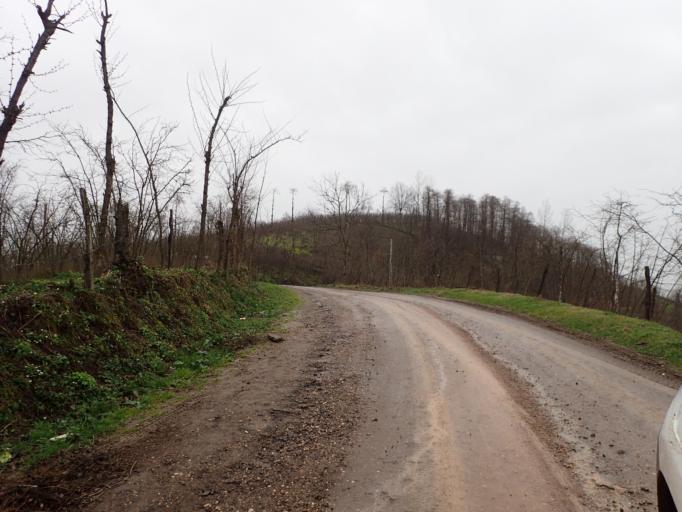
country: TR
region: Ordu
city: Camas
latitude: 40.8809
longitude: 37.5004
